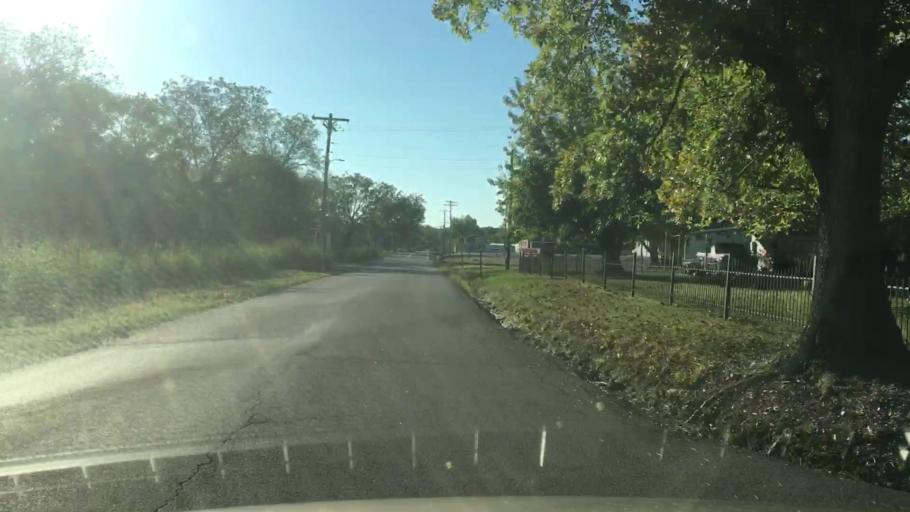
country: US
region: Oklahoma
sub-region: Muskogee County
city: Fort Gibson
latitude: 35.9297
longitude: -95.1427
